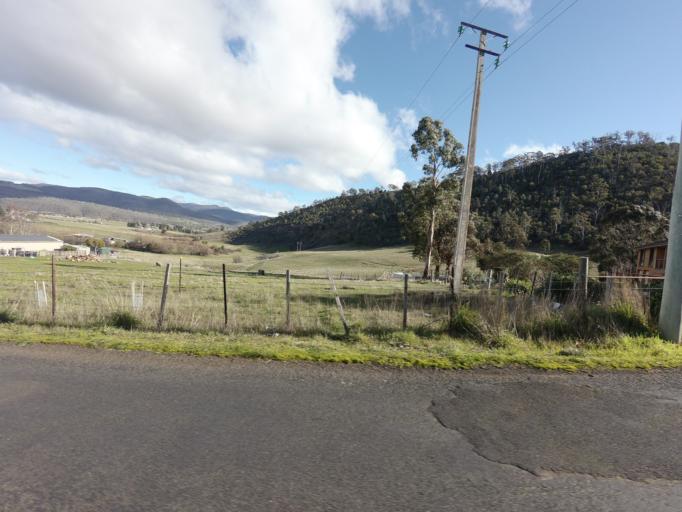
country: AU
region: Tasmania
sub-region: Derwent Valley
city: New Norfolk
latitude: -42.7519
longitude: 147.0467
